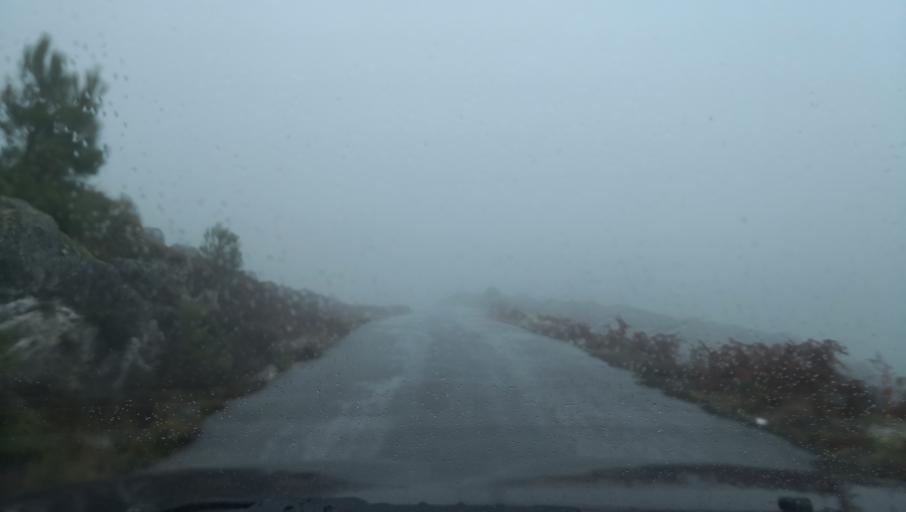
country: PT
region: Vila Real
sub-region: Vila Real
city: Vila Real
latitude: 41.3259
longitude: -7.7898
